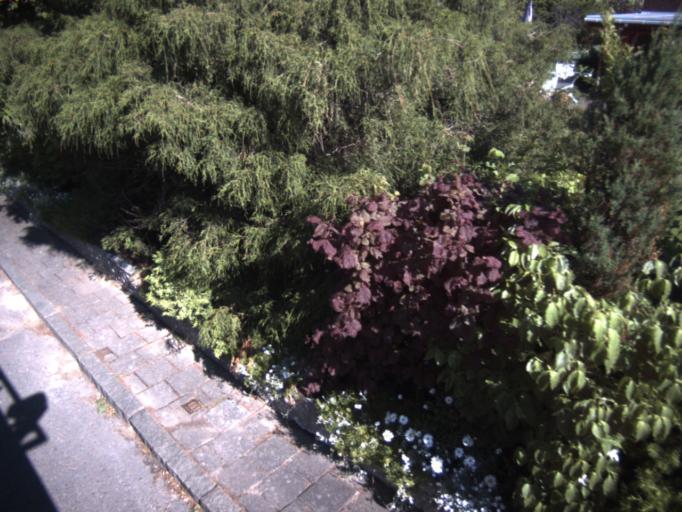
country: SE
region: Skane
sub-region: Helsingborg
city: Helsingborg
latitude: 56.0245
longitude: 12.7479
